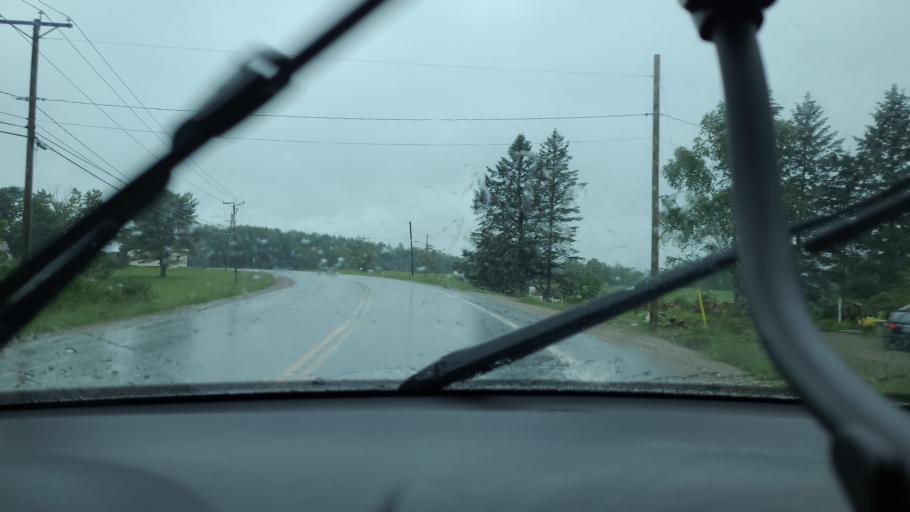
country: CA
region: Quebec
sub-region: Outaouais
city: Saint-Andre-Avellin
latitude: 45.8360
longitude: -75.0615
